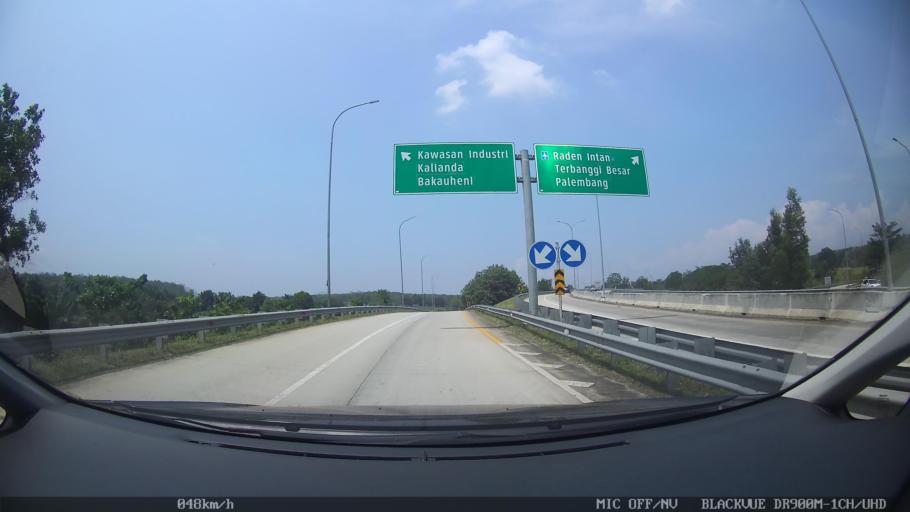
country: ID
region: Lampung
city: Kedaton
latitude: -5.3649
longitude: 105.3282
